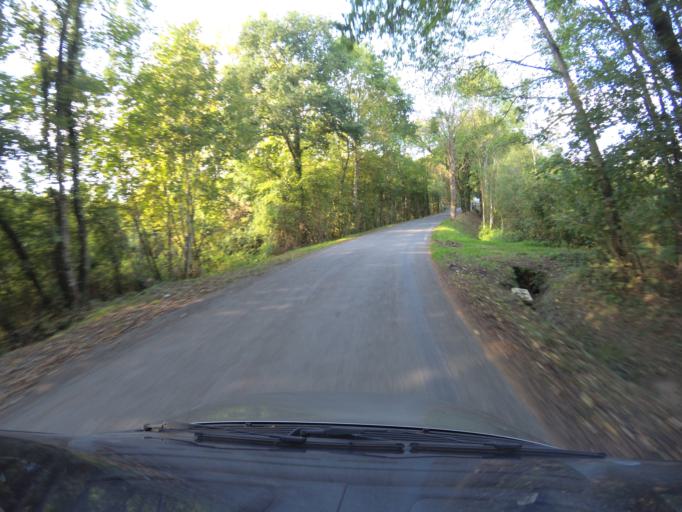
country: FR
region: Brittany
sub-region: Departement du Morbihan
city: Saint-Vincent-sur-Oust
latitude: 47.7191
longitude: -2.1698
